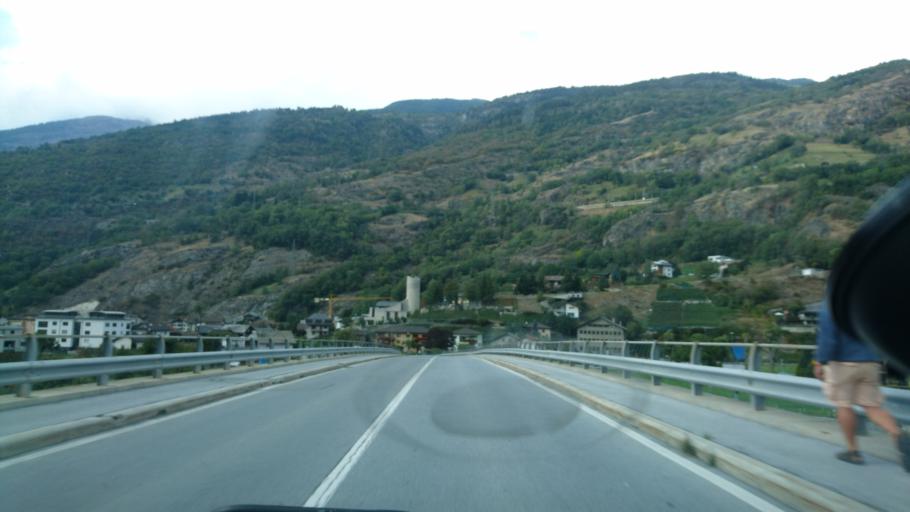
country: CH
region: Valais
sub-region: Visp District
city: Visp
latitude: 46.2963
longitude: 7.9052
